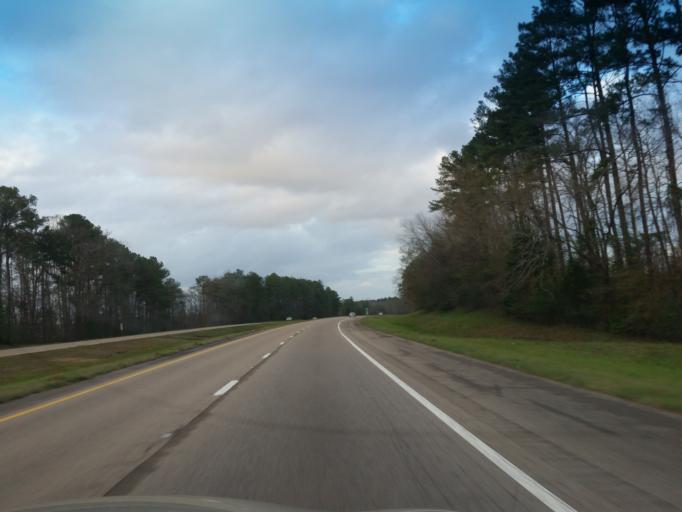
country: US
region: Mississippi
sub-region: Clarke County
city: Stonewall
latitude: 32.0401
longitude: -88.9208
